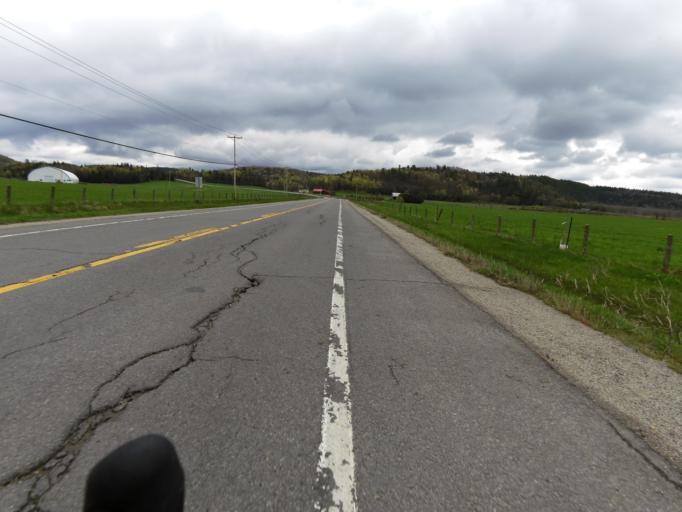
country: CA
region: Quebec
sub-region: Outaouais
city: Wakefield
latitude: 45.6438
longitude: -75.8953
